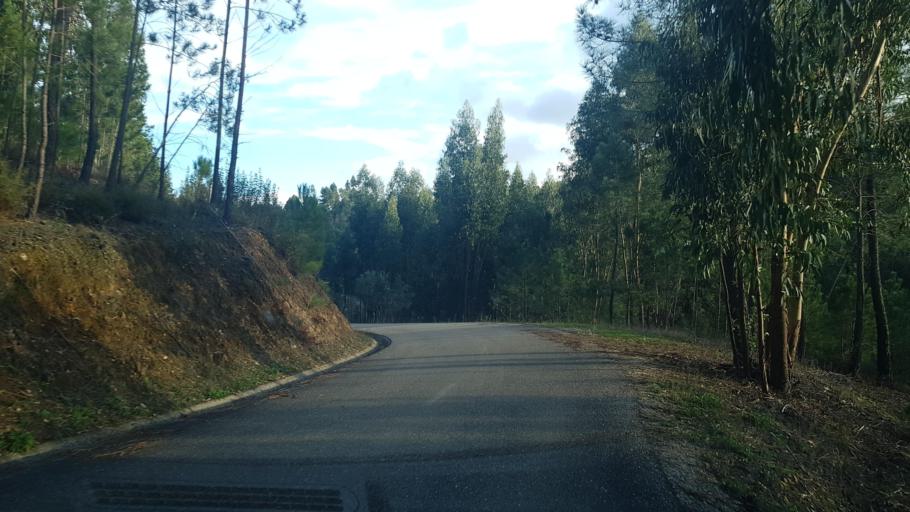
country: PT
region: Castelo Branco
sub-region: Vila de Rei
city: Vila de Rei
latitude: 39.5990
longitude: -8.1195
